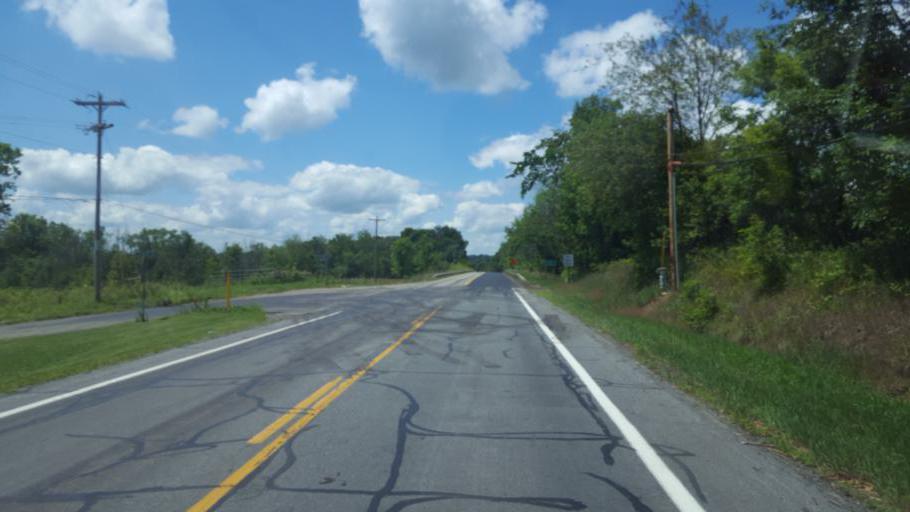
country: US
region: Ohio
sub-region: Richland County
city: Lexington
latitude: 40.6376
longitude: -82.6382
